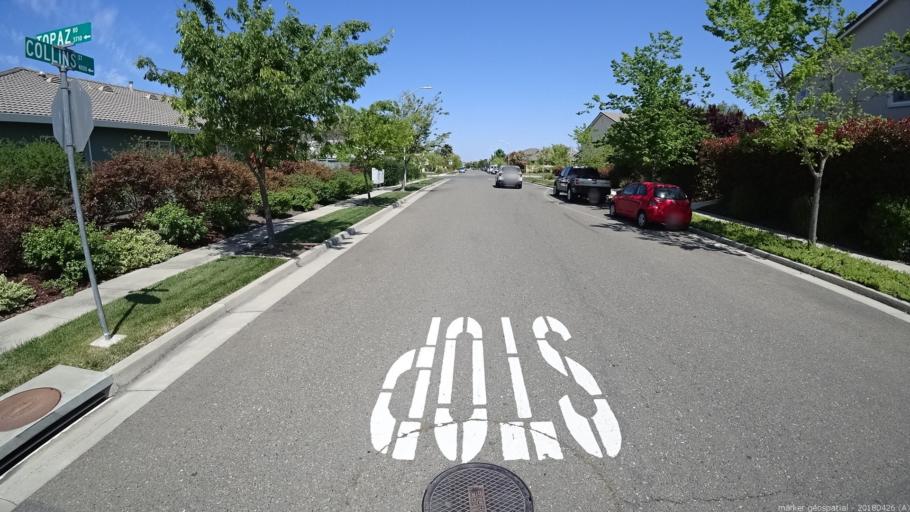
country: US
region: California
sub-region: Yolo County
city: West Sacramento
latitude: 38.5241
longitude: -121.5768
